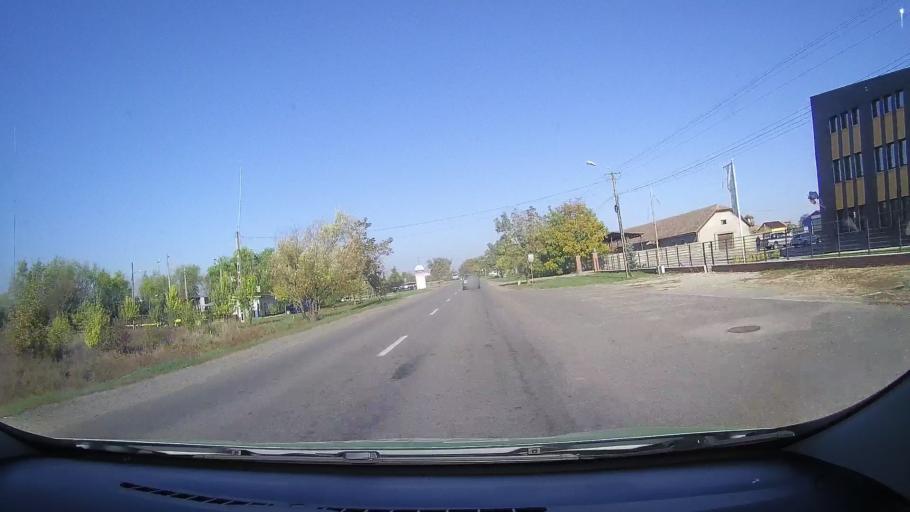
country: RO
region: Satu Mare
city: Carei
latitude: 47.6725
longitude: 22.4831
